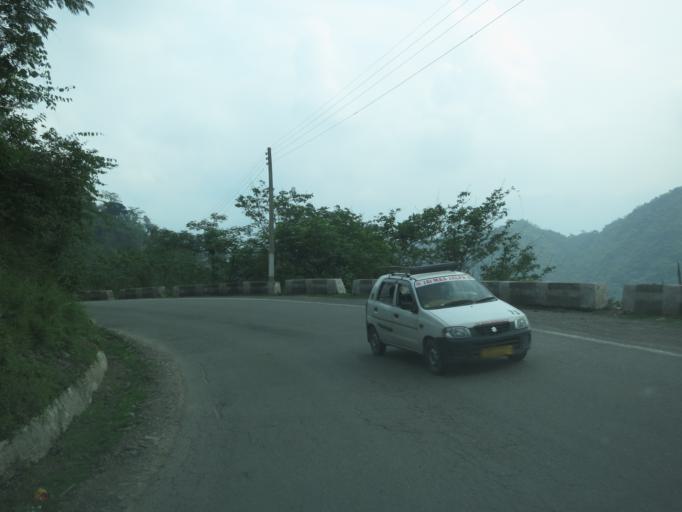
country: IN
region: Himachal Pradesh
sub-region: Solan
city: Arki
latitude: 31.2519
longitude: 76.8732
